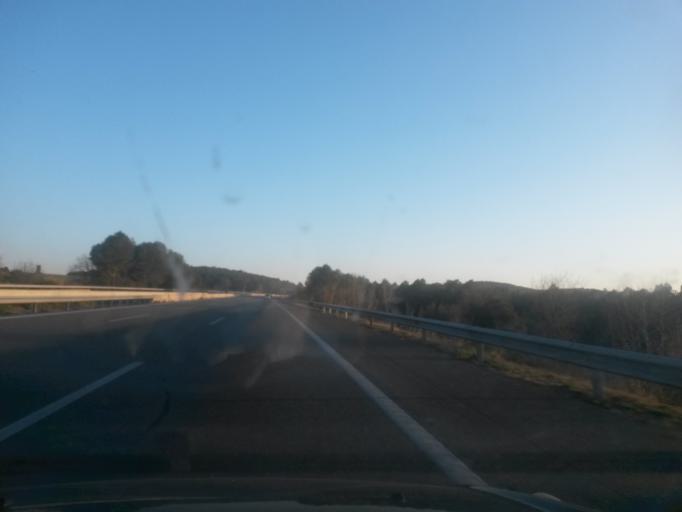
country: ES
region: Catalonia
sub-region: Provincia de Girona
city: Bascara
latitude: 42.1516
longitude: 2.9174
